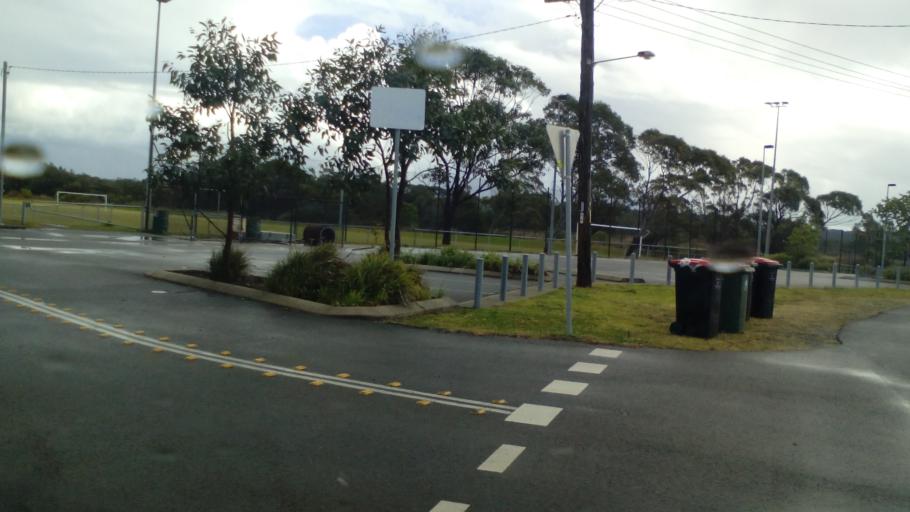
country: AU
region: New South Wales
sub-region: Lake Macquarie Shire
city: Redhead
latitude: -33.0091
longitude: 151.7069
